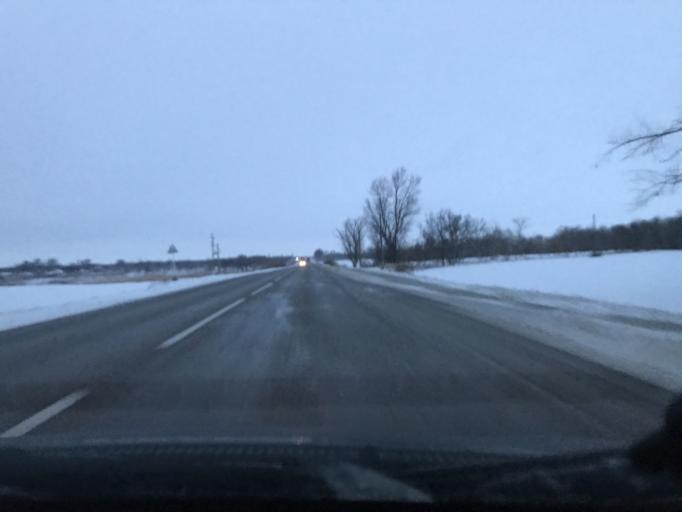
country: RU
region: Rostov
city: Letnik
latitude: 45.9333
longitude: 41.2886
